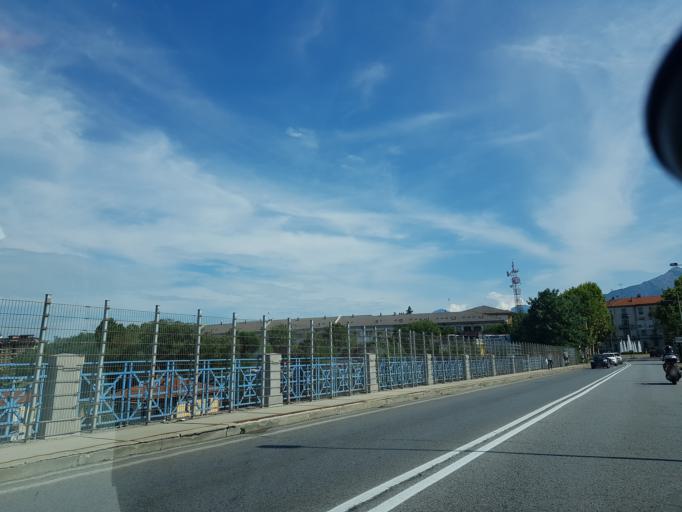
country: IT
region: Piedmont
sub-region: Provincia di Cuneo
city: Cuneo
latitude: 44.3924
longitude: 7.5420
